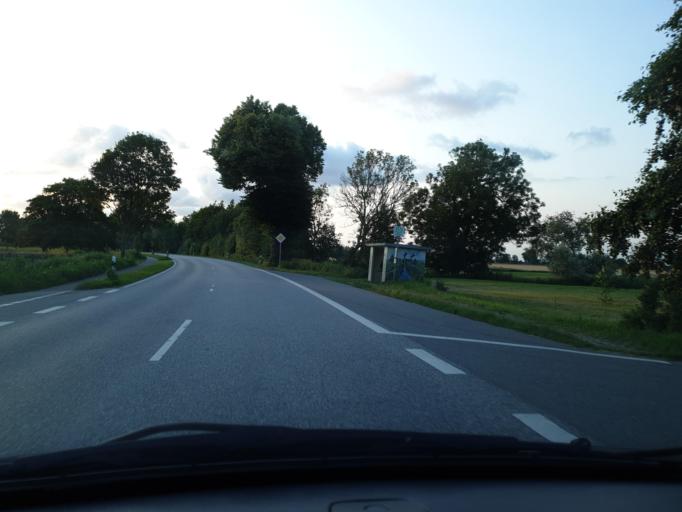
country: DE
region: Schleswig-Holstein
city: Diekhusen-Fahrstedt
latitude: 53.9327
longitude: 9.0340
